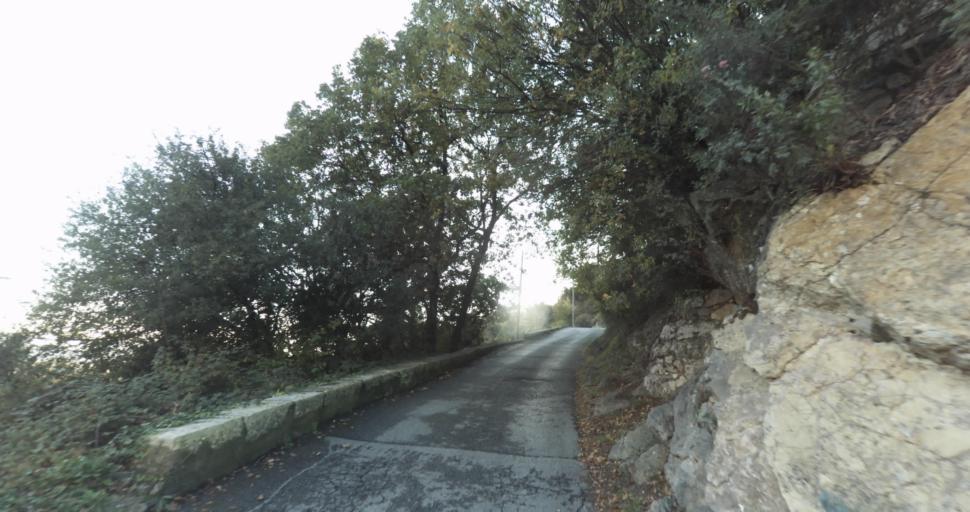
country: FR
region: Provence-Alpes-Cote d'Azur
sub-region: Departement des Alpes-Maritimes
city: Vence
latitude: 43.7328
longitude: 7.1032
